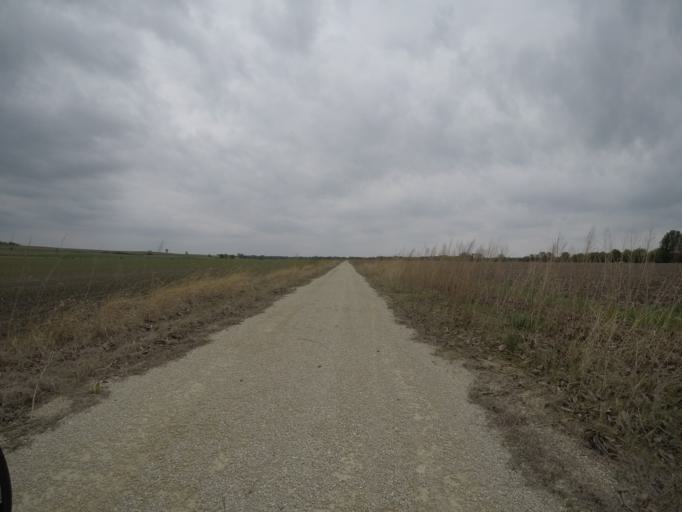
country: US
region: Nebraska
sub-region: Gage County
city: Wymore
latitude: 40.0852
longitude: -96.5940
